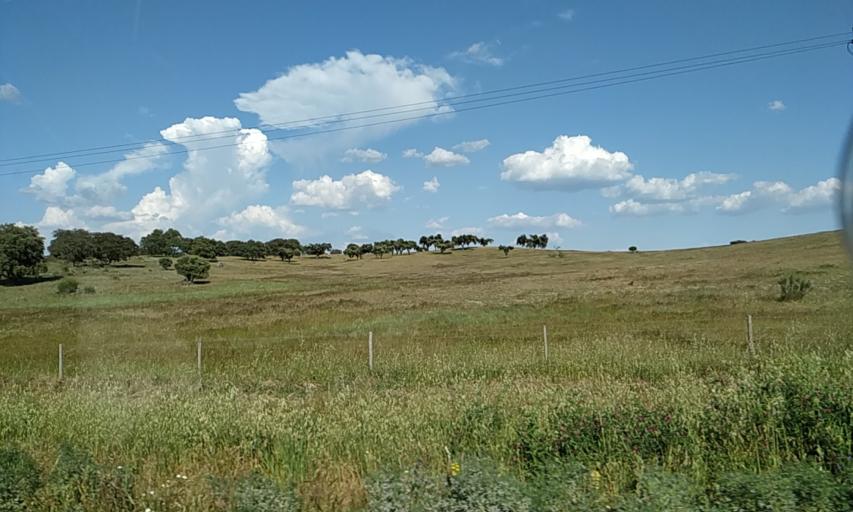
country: PT
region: Portalegre
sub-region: Fronteira
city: Fronteira
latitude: 39.0160
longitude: -7.4660
